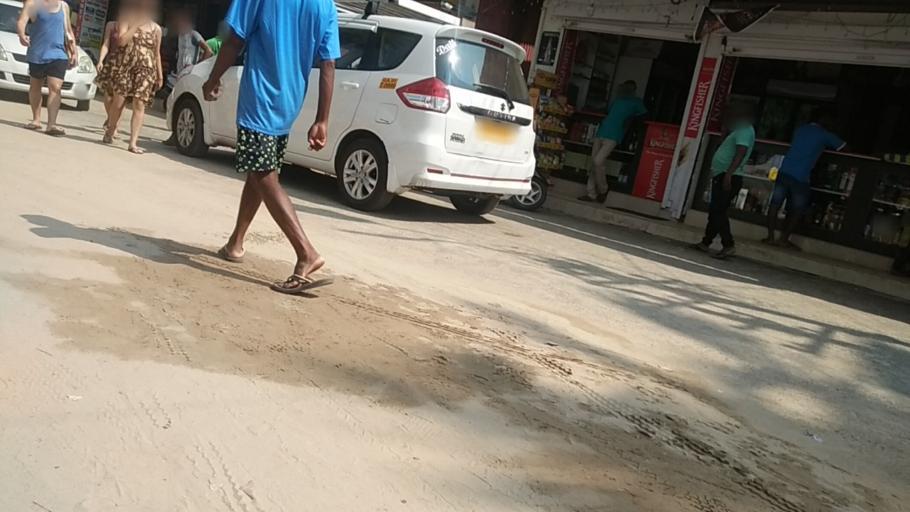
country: IN
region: Goa
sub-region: South Goa
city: Kankon
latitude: 15.0116
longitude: 74.0215
